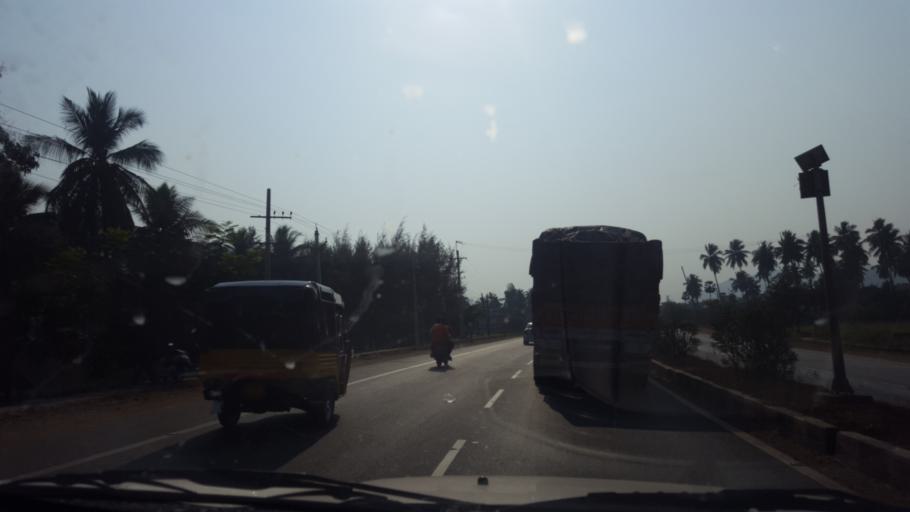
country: IN
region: Andhra Pradesh
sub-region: Vishakhapatnam
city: Anakapalle
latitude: 17.6613
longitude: 82.9417
